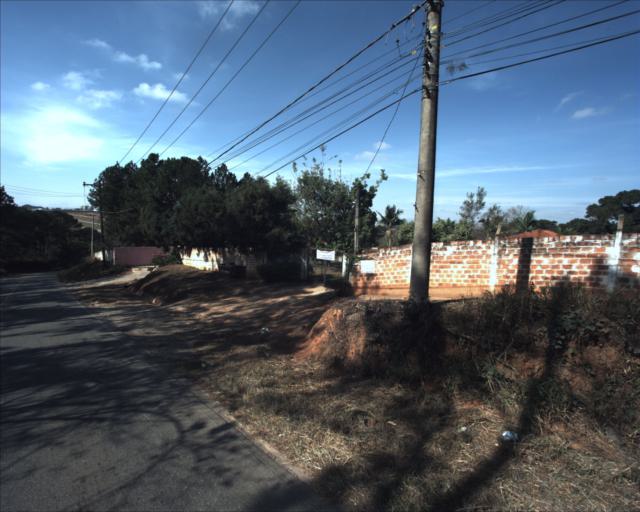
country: BR
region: Sao Paulo
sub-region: Sorocaba
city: Sorocaba
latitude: -23.4424
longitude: -47.5240
